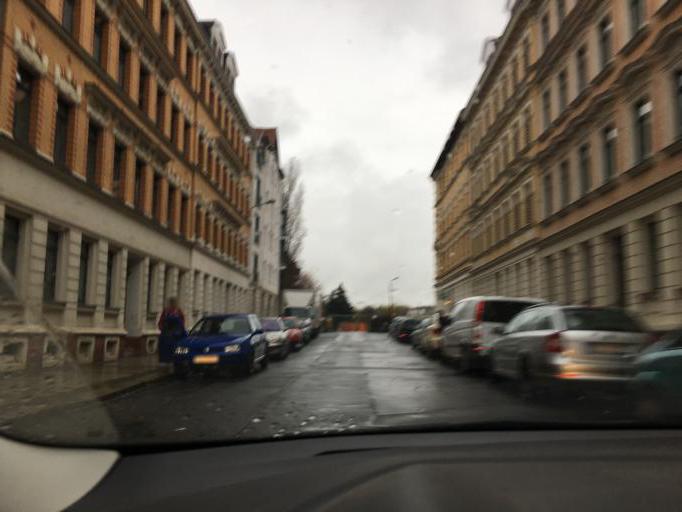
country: DE
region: Saxony
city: Leipzig
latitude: 51.3408
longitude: 12.4124
